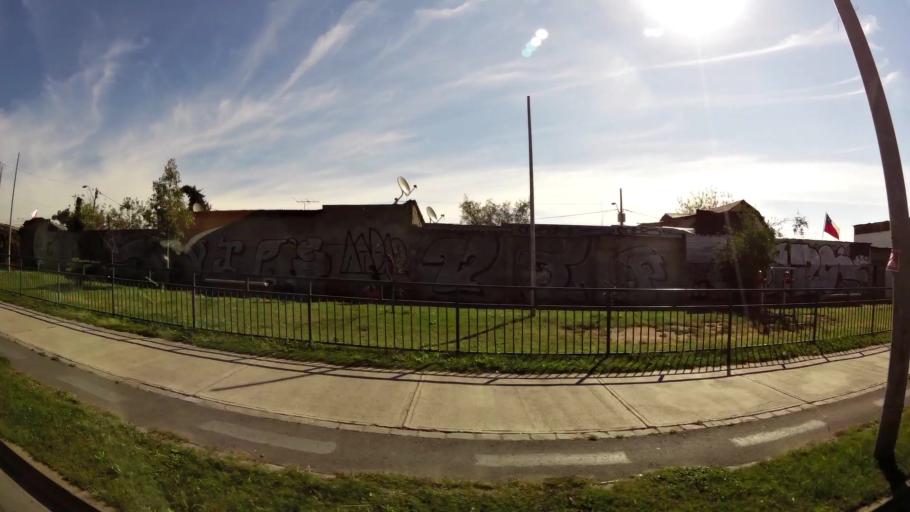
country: CL
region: Santiago Metropolitan
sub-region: Provincia de Santiago
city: Santiago
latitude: -33.4883
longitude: -70.6299
